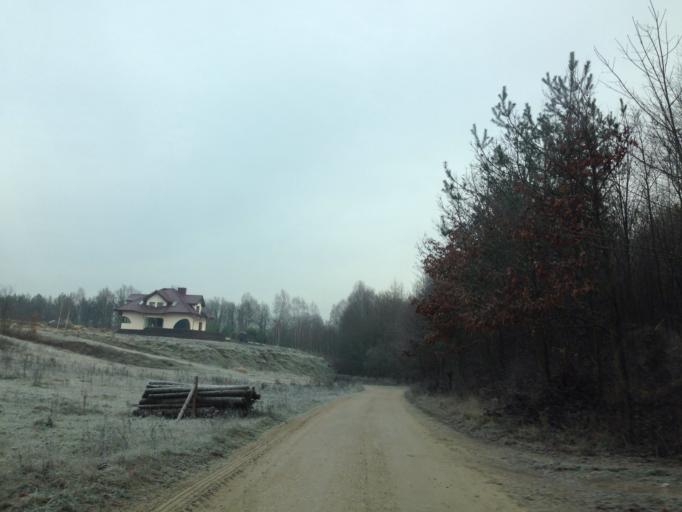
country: PL
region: Kujawsko-Pomorskie
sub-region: Powiat brodnicki
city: Gorzno
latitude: 53.2232
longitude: 19.6480
